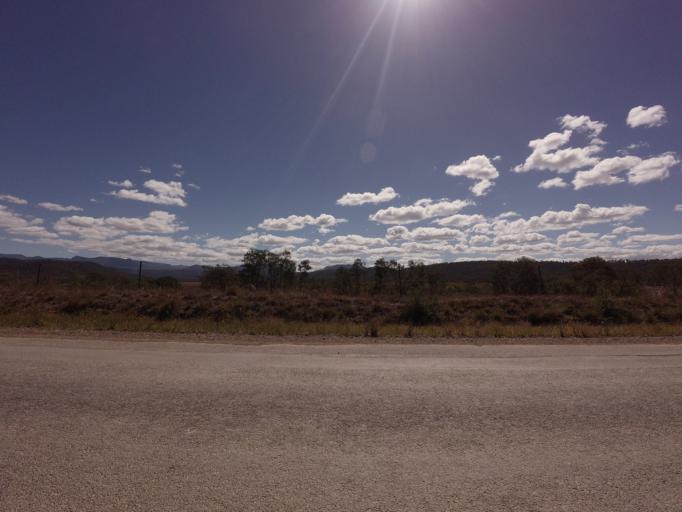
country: AU
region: Tasmania
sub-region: Break O'Day
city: St Helens
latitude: -41.6476
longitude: 147.9360
